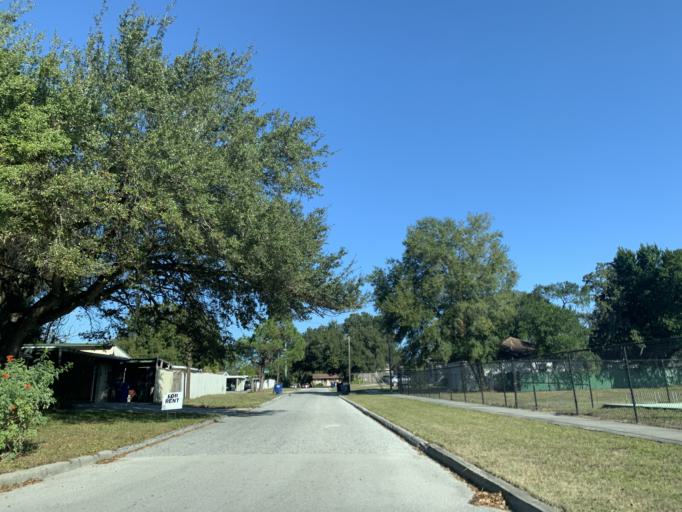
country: US
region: Florida
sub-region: Hillsborough County
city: Temple Terrace
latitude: 28.0275
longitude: -82.4110
